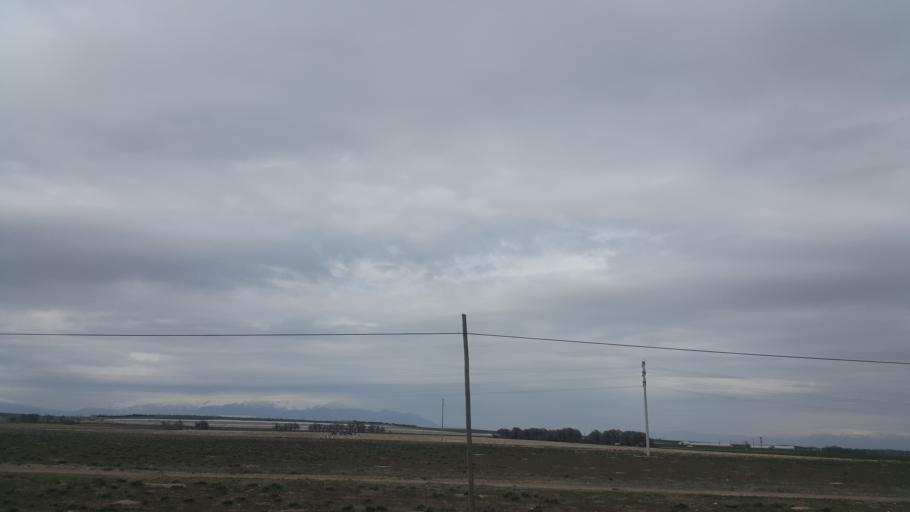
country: TR
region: Nigde
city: Altunhisar
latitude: 37.7946
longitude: 34.2244
